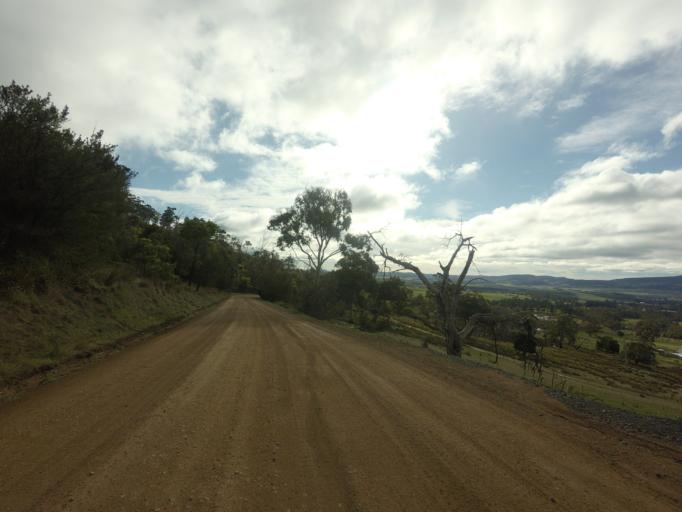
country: AU
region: Tasmania
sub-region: Derwent Valley
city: New Norfolk
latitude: -42.7252
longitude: 146.8721
